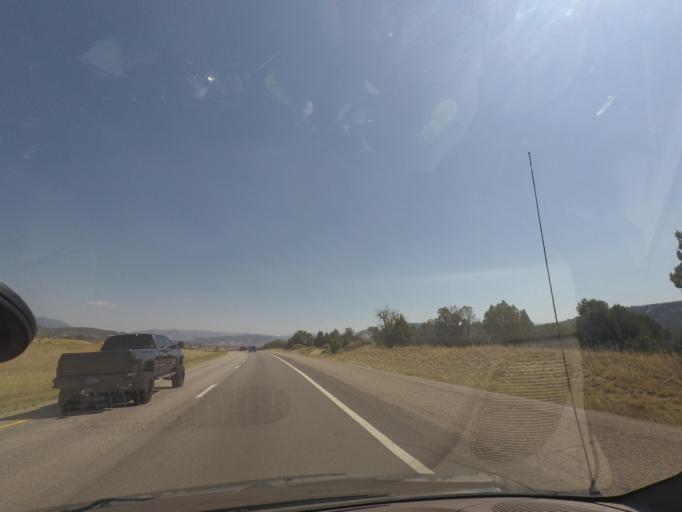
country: US
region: Colorado
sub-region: Eagle County
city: Eagle
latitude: 39.6523
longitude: -106.8821
